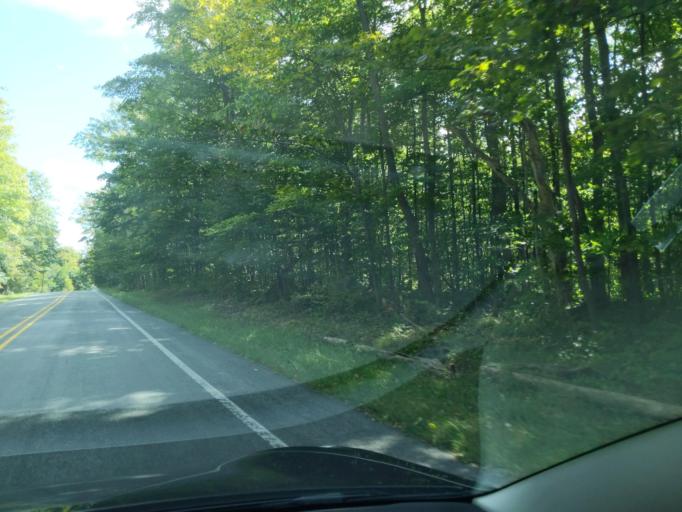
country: US
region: Michigan
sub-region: Antrim County
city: Bellaire
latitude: 44.9987
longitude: -85.2909
